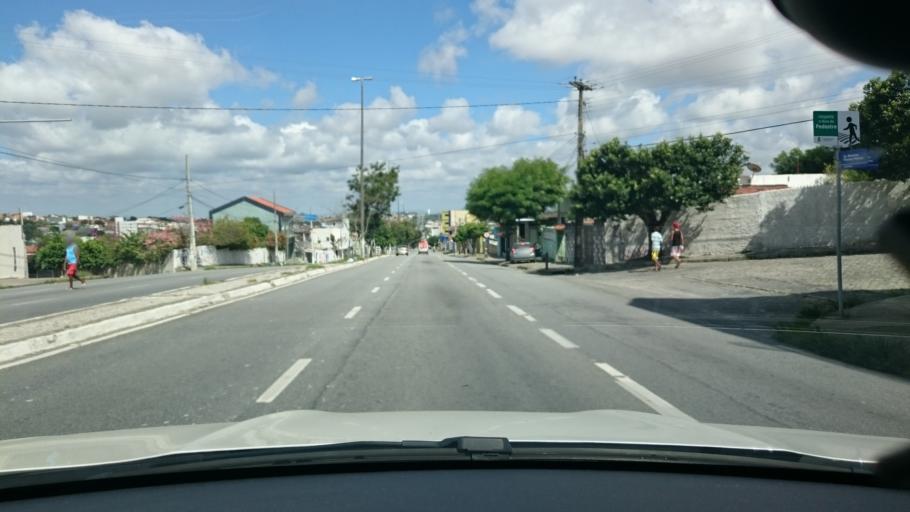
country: BR
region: Paraiba
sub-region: Campina Grande
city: Campina Grande
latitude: -7.2265
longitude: -35.8991
